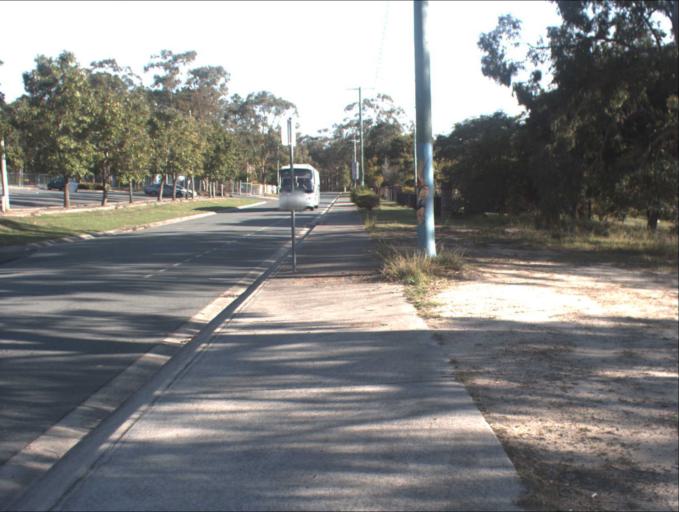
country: AU
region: Queensland
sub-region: Logan
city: Park Ridge South
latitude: -27.6999
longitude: 153.0332
